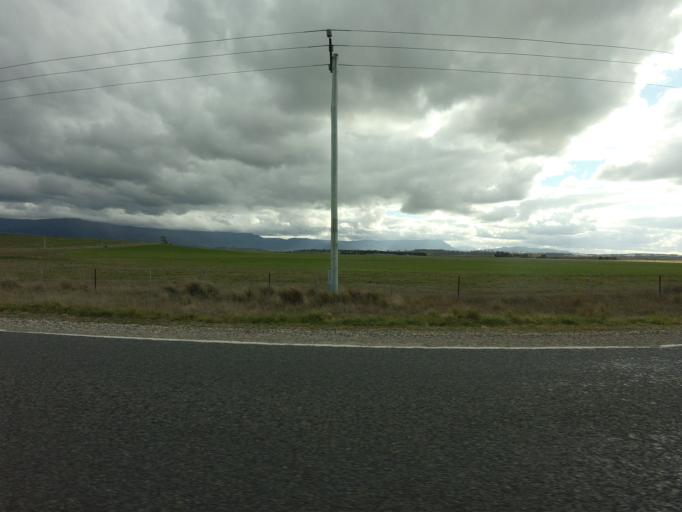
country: AU
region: Tasmania
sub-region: Northern Midlands
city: Longford
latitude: -41.7541
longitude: 147.0825
